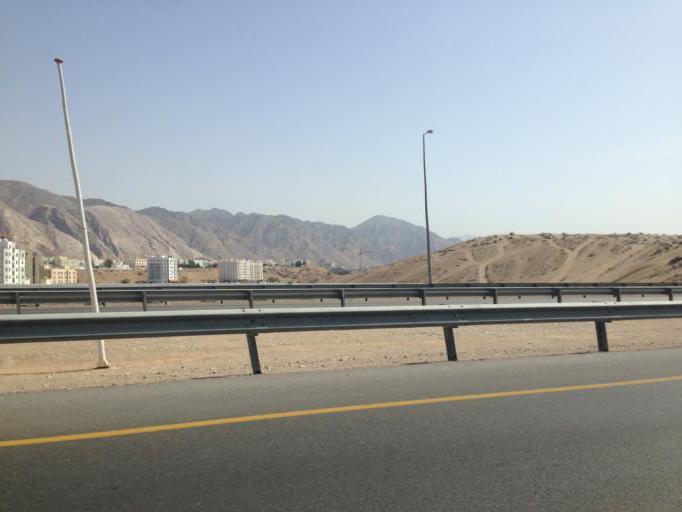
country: OM
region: Muhafazat Masqat
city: Bawshar
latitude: 23.5701
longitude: 58.4130
